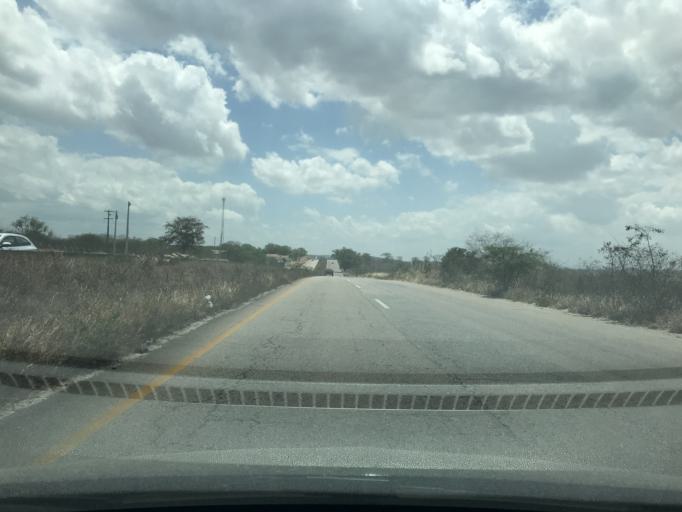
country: BR
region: Pernambuco
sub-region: Caruaru
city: Caruaru
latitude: -8.2972
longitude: -35.8973
